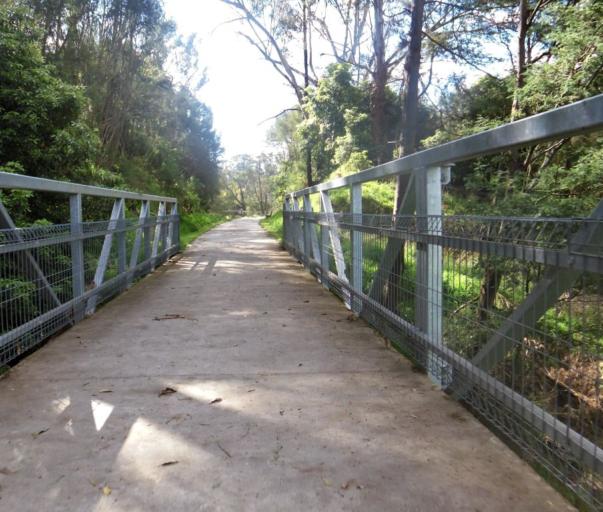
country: AU
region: Victoria
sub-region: Bass Coast
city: North Wonthaggi
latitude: -38.5599
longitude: 145.9541
